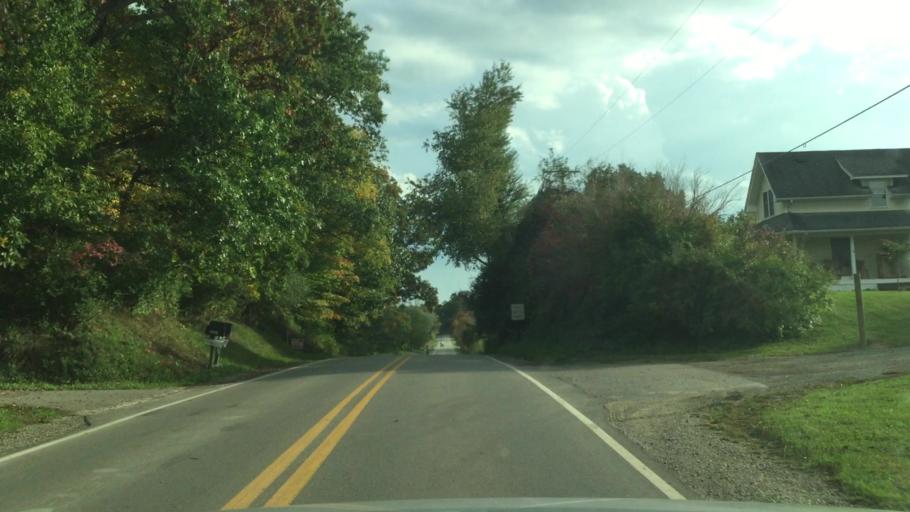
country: US
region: Michigan
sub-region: Genesee County
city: Fenton
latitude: 42.6833
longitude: -83.7025
